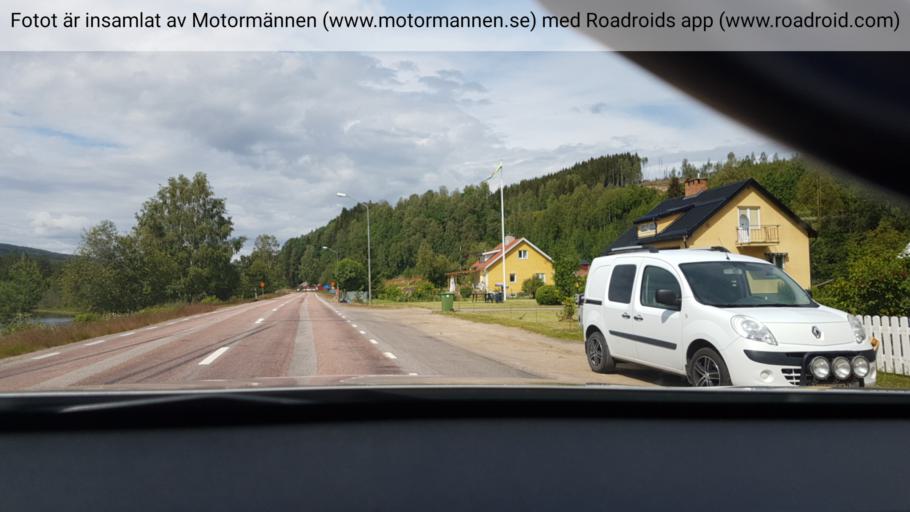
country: SE
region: Vaermland
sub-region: Torsby Kommun
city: Torsby
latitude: 60.7393
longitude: 12.8527
